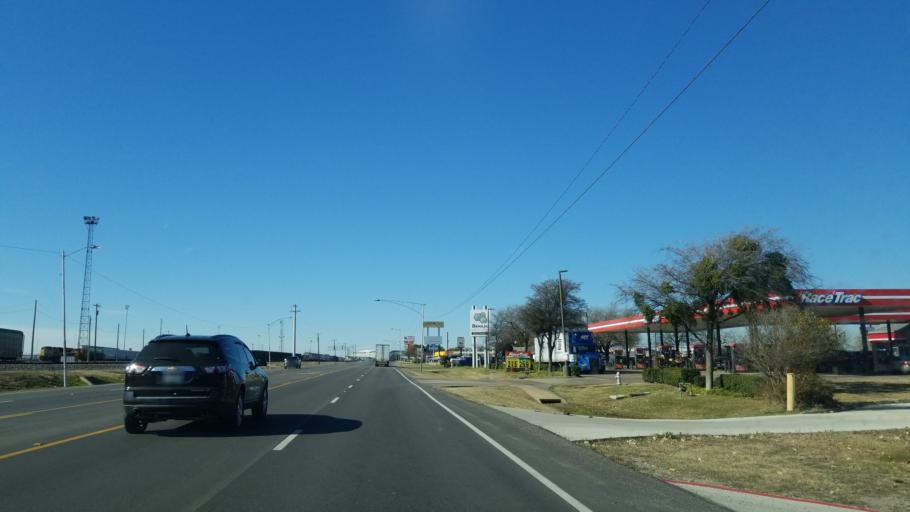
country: US
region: Texas
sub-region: Dallas County
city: Grand Prairie
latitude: 32.7400
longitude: -97.0484
